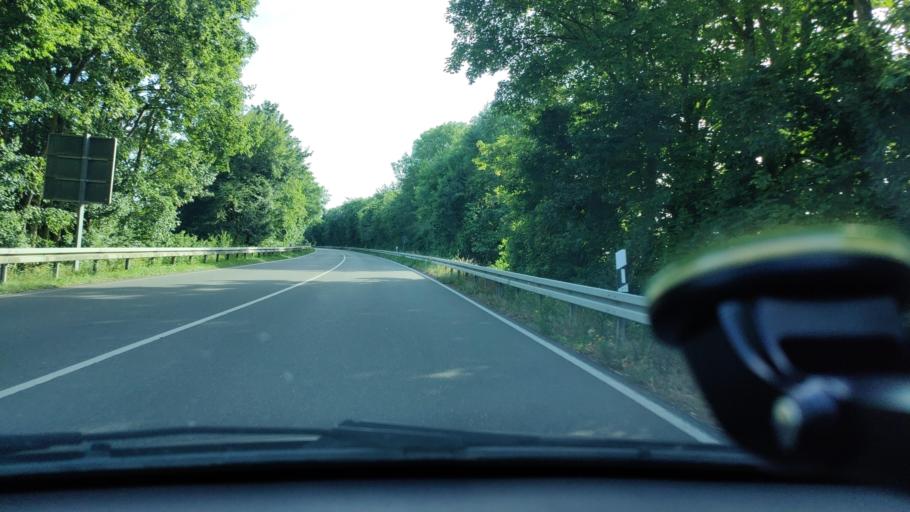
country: DE
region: North Rhine-Westphalia
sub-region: Regierungsbezirk Munster
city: Billerbeck
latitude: 52.0207
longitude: 7.2285
